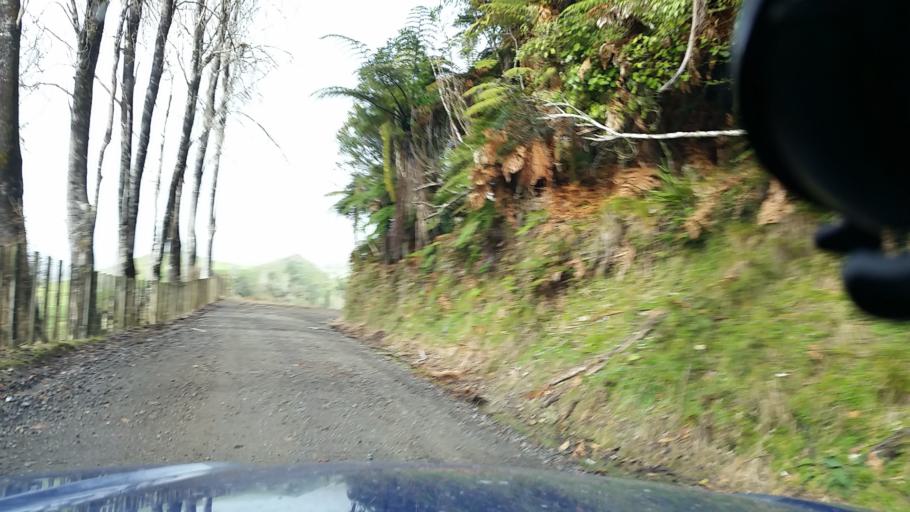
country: NZ
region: Taranaki
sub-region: New Plymouth District
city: Waitara
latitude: -39.0033
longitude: 174.7644
